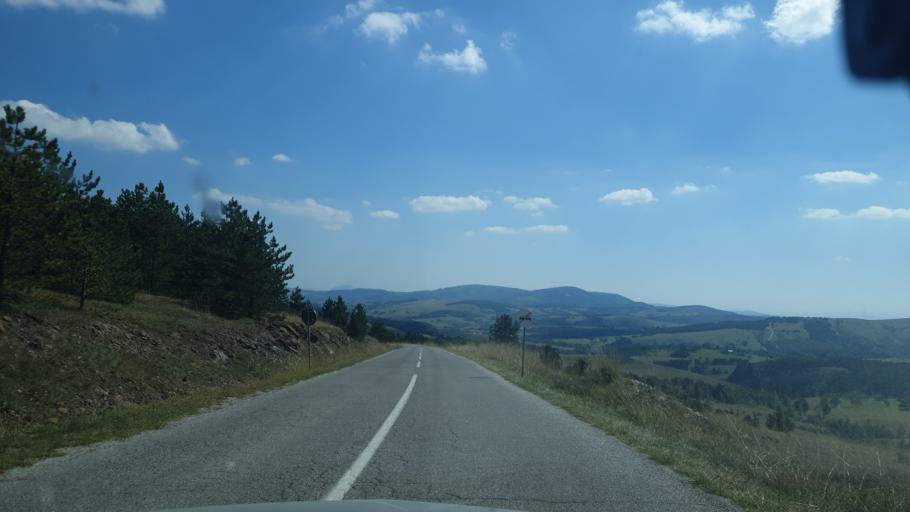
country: RS
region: Central Serbia
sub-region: Zlatiborski Okrug
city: Kosjeric
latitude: 44.0822
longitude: 20.0148
